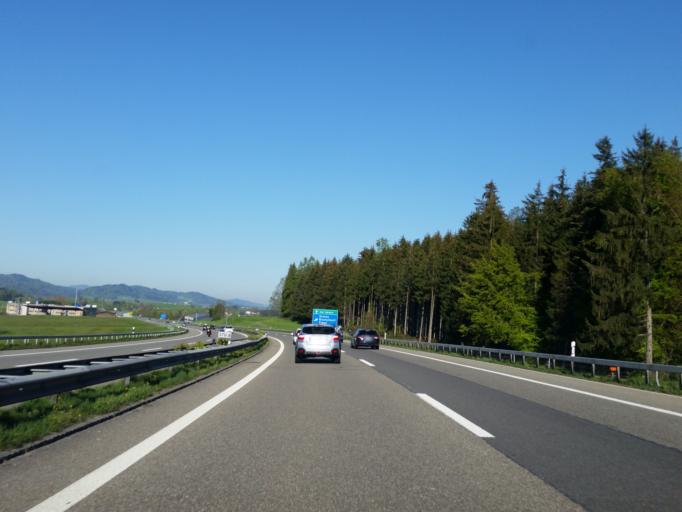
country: CH
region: Saint Gallen
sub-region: Wahlkreis St. Gallen
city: Gossau
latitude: 47.4265
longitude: 9.2513
